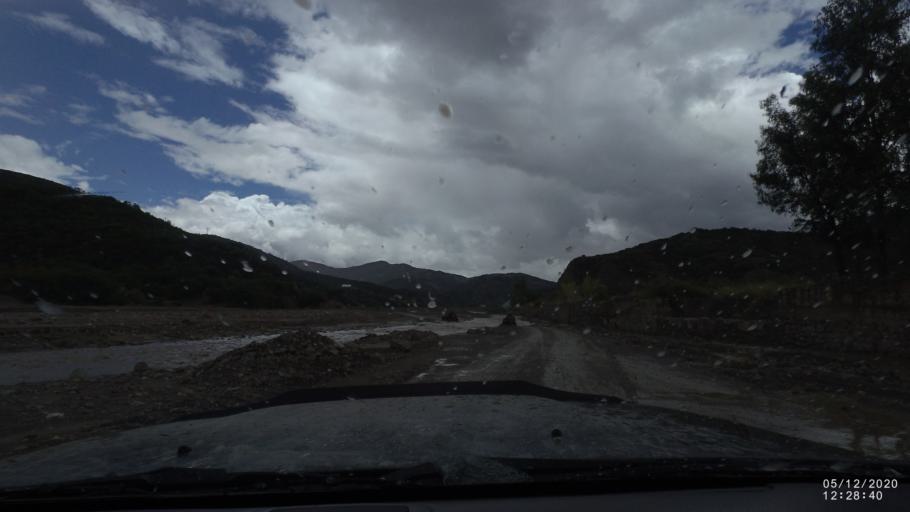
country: BO
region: Cochabamba
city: Sipe Sipe
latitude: -17.5471
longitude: -66.4131
